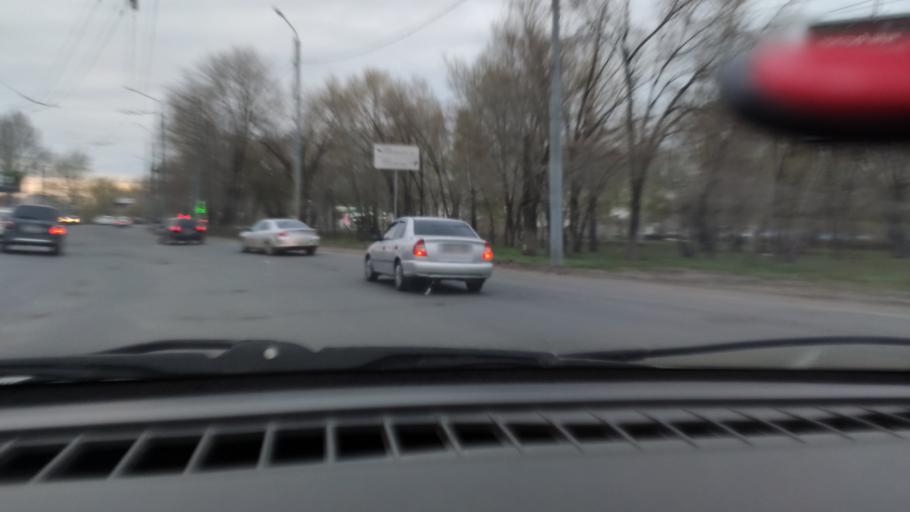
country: RU
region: Orenburg
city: Orenburg
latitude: 51.8117
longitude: 55.1448
